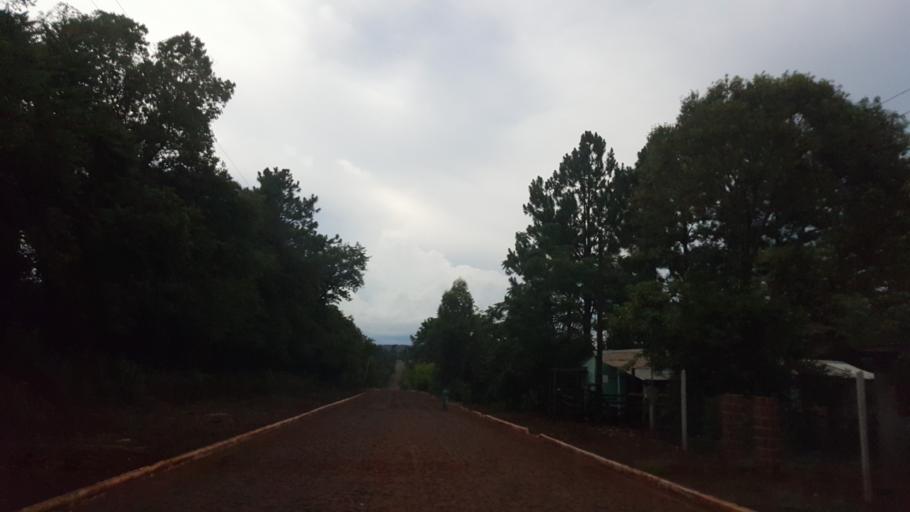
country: AR
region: Misiones
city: Jardin America
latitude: -27.0770
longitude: -55.2864
